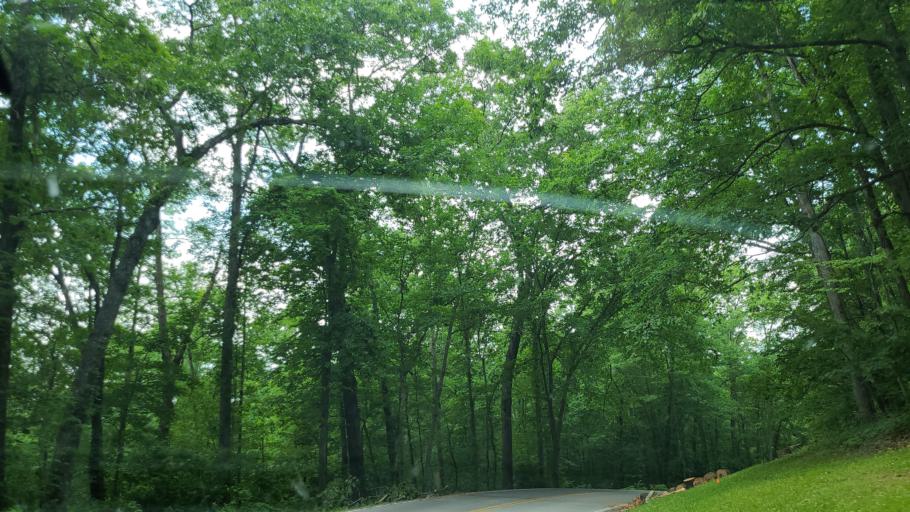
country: US
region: Tennessee
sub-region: Cumberland County
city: Crossville
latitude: 35.8985
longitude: -84.9954
